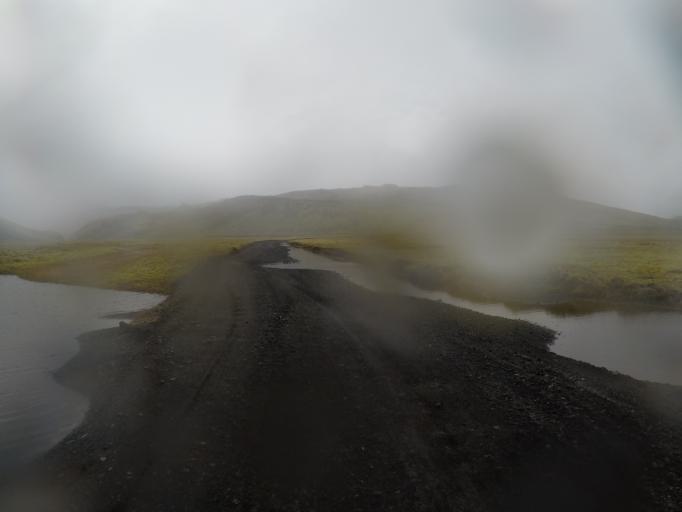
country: IS
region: South
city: Vestmannaeyjar
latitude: 63.9744
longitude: -18.8388
